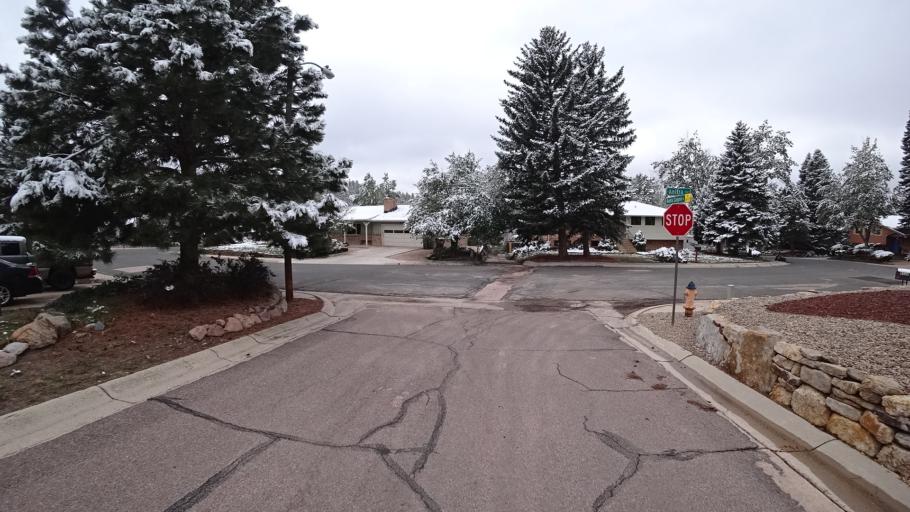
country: US
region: Colorado
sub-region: El Paso County
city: Colorado Springs
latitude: 38.8927
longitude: -104.7782
